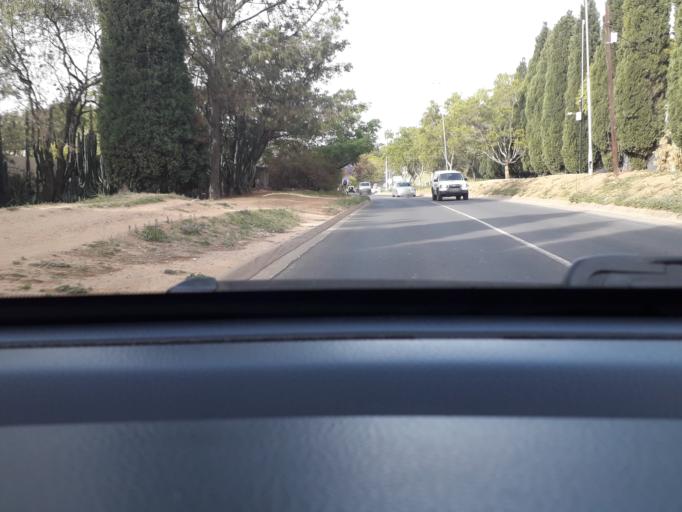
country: ZA
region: Gauteng
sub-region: City of Johannesburg Metropolitan Municipality
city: Diepsloot
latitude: -26.0368
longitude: 27.9991
